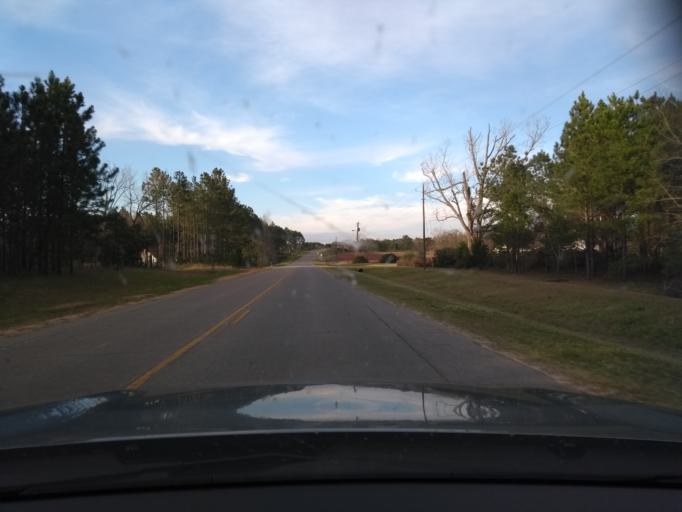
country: US
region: Georgia
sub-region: Bulloch County
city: Brooklet
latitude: 32.2710
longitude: -81.7597
